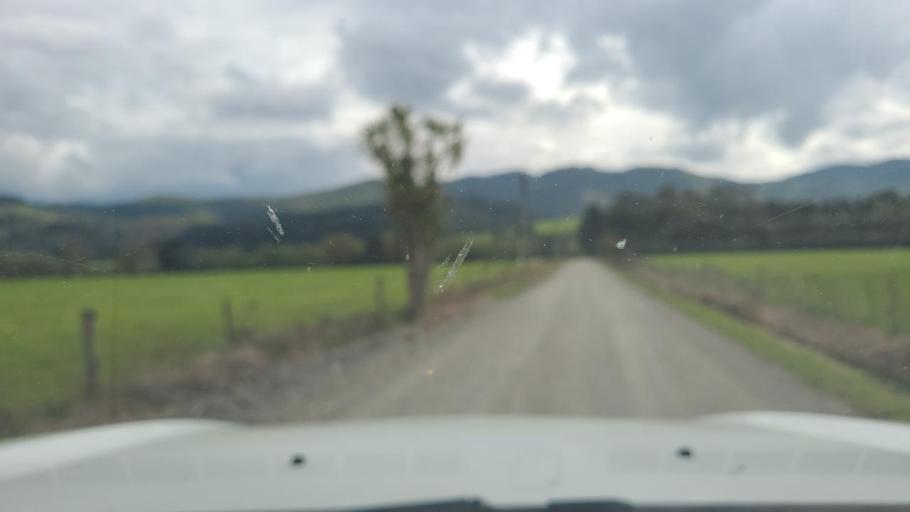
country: NZ
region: Wellington
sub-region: Masterton District
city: Masterton
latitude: -40.9932
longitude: 175.4990
